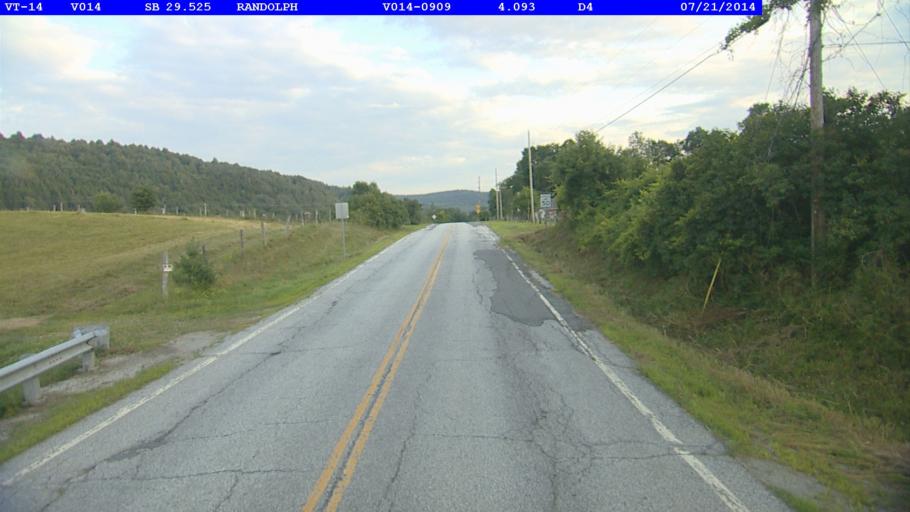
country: US
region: Vermont
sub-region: Orange County
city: Randolph
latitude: 43.9283
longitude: -72.5530
